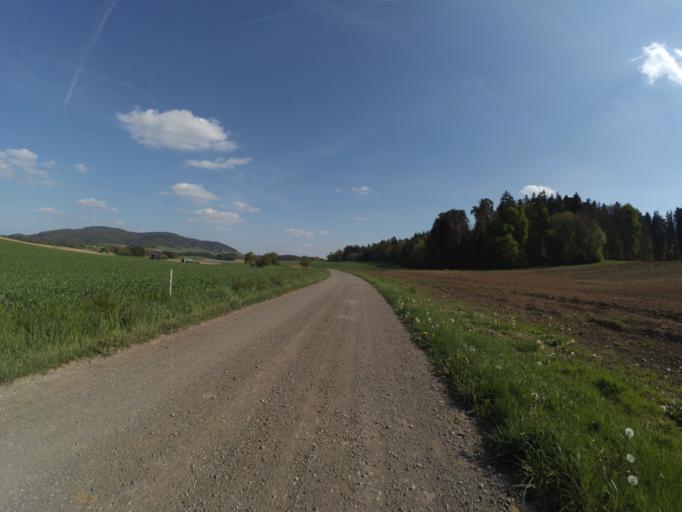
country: CH
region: Thurgau
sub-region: Frauenfeld District
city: Diessenhofen
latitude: 47.6587
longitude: 8.7559
